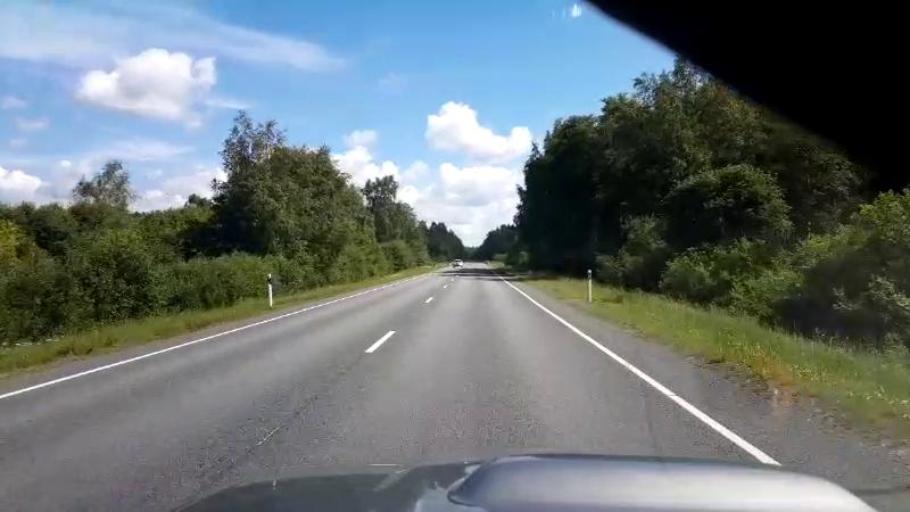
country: EE
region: Laeaene-Virumaa
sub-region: Tapa vald
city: Tapa
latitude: 59.1962
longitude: 25.8293
